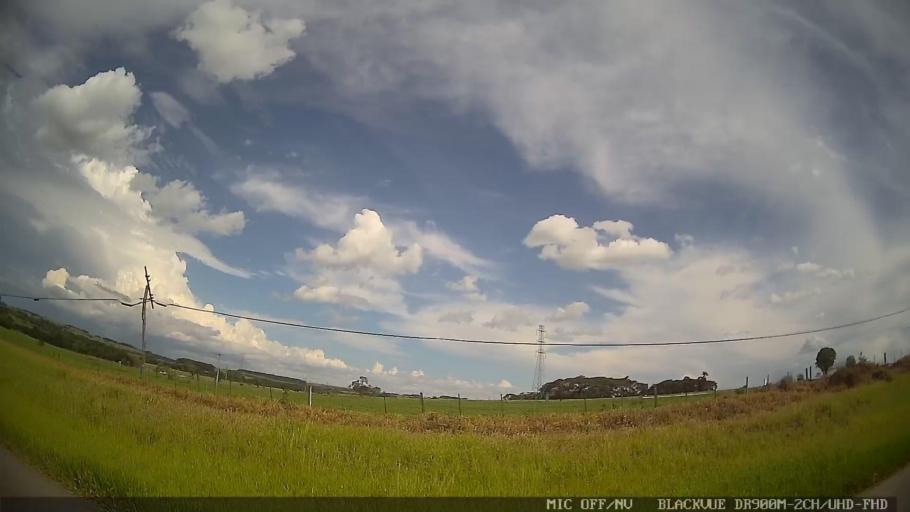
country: BR
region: Sao Paulo
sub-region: Conchas
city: Conchas
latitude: -23.0589
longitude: -47.9650
